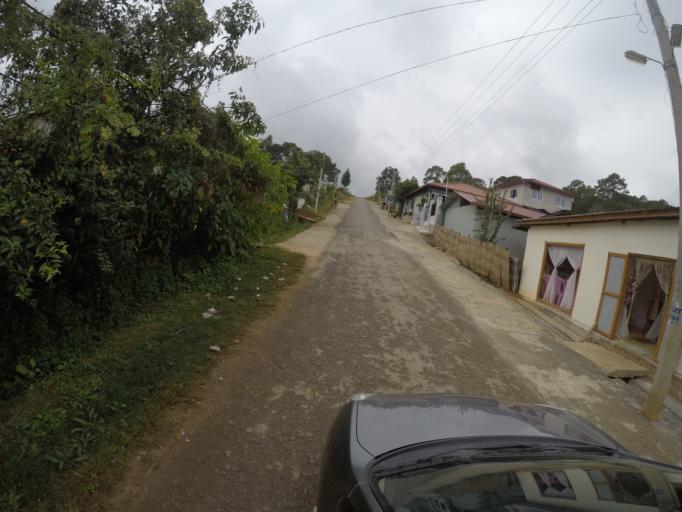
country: MM
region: Shan
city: Taunggyi
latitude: 20.6523
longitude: 96.6256
